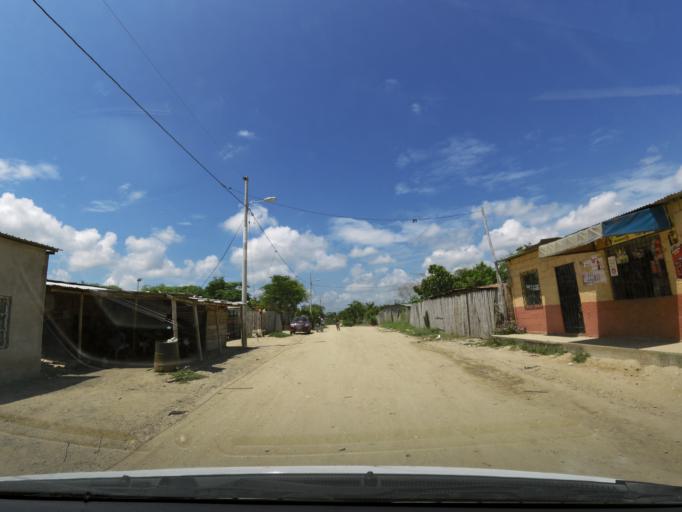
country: EC
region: El Oro
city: Huaquillas
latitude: -3.4732
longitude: -80.2120
